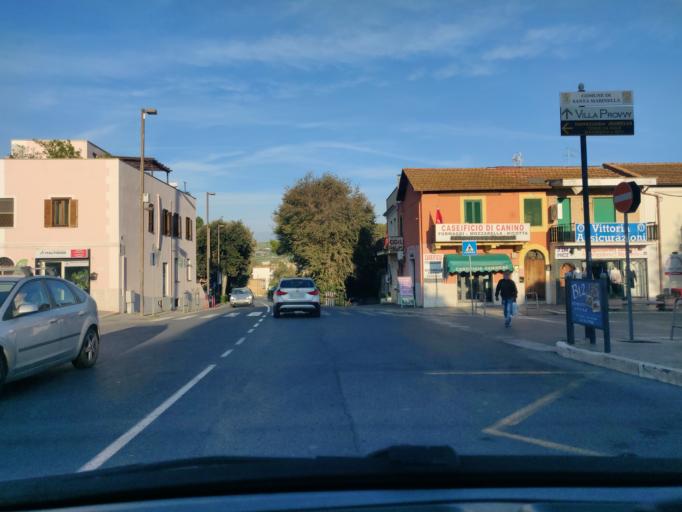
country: IT
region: Latium
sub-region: Citta metropolitana di Roma Capitale
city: Santa Marinella
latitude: 42.0361
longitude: 11.8686
